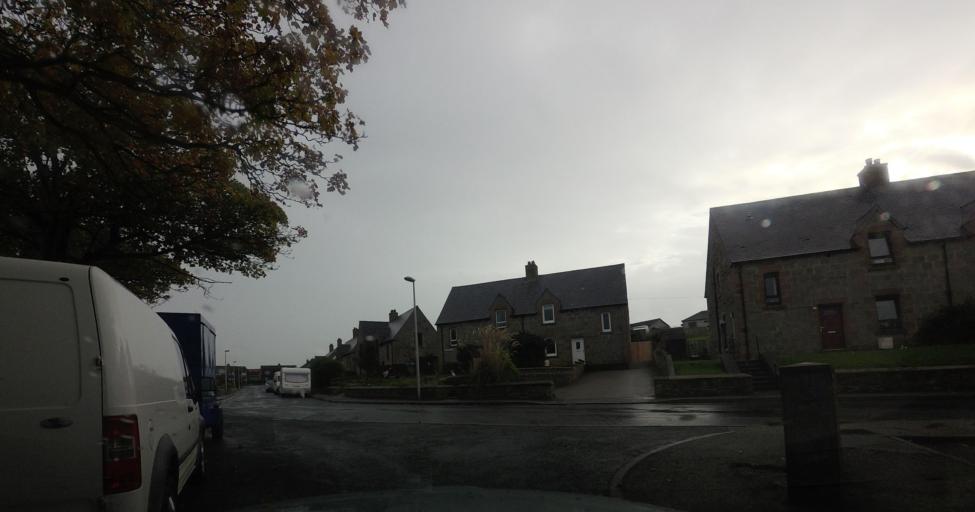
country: GB
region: Scotland
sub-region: Aberdeenshire
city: Macduff
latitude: 57.6668
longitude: -2.4975
